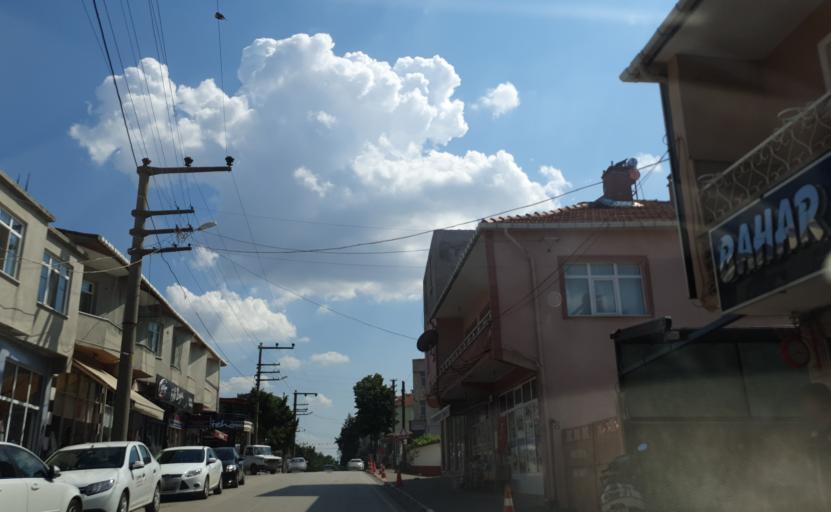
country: TR
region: Kirklareli
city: Buyukkaristiran
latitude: 41.4393
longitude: 27.5854
